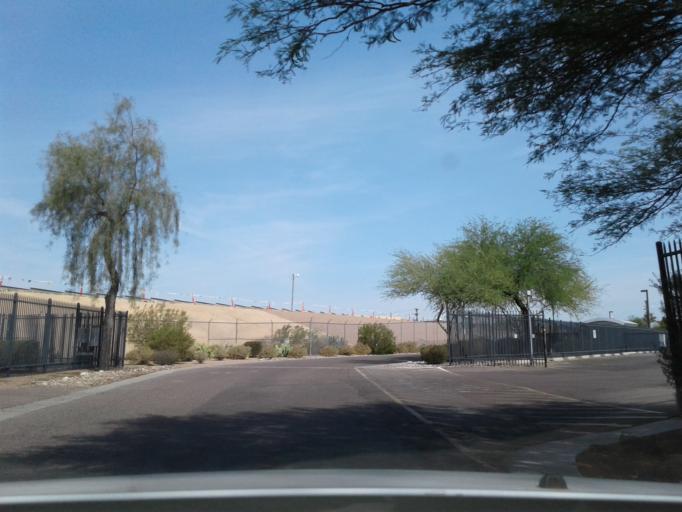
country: US
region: Arizona
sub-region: Maricopa County
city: Paradise Valley
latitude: 33.5275
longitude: -112.0310
